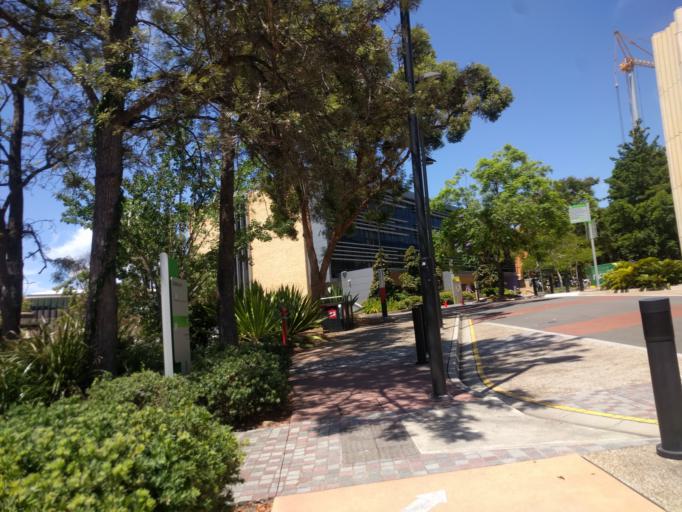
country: AU
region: Queensland
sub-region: Brisbane
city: Yeronga
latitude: -27.4984
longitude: 153.0144
